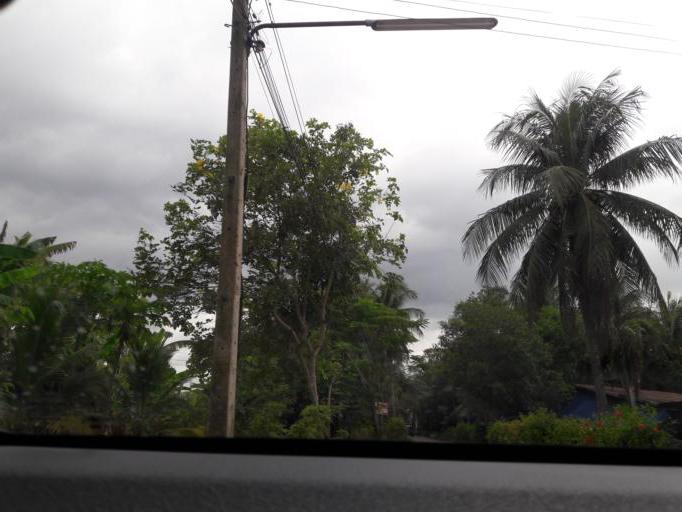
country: TH
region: Ratchaburi
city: Damnoen Saduak
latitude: 13.5732
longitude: 99.9944
